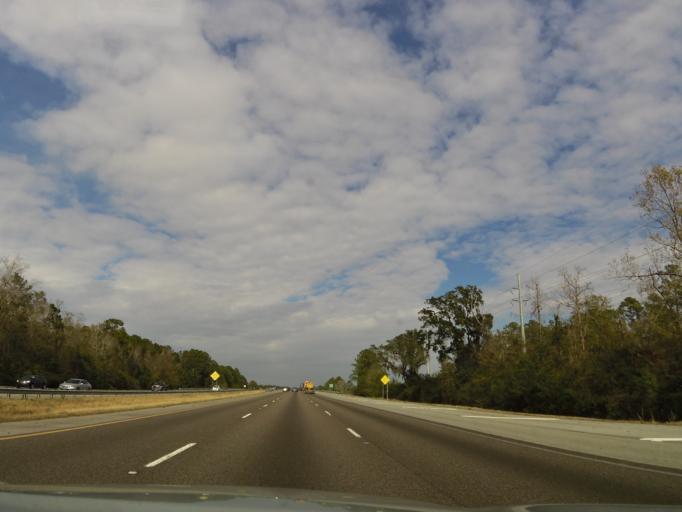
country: US
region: Georgia
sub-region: Liberty County
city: Midway
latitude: 31.8179
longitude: -81.3611
